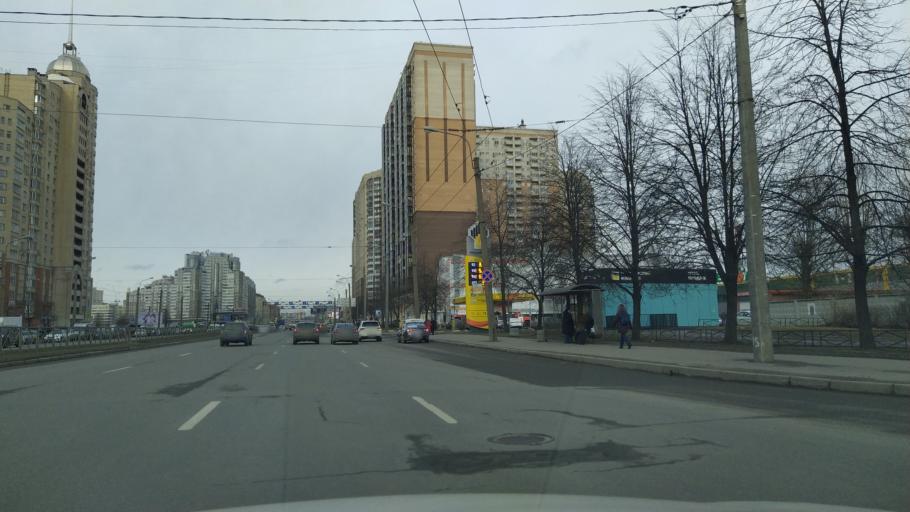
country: RU
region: Leningrad
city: Chernaya Rechka
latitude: 59.9979
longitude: 30.2999
